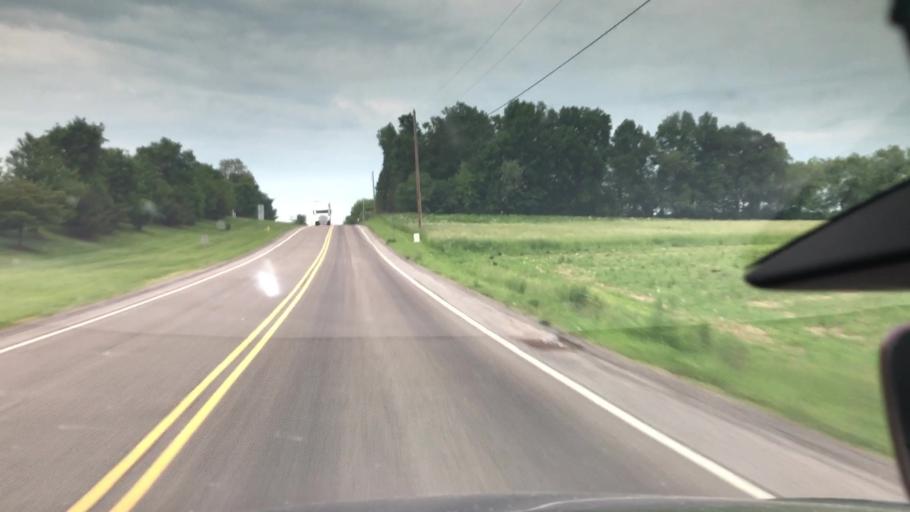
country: US
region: Pennsylvania
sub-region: Butler County
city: Saxonburg
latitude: 40.7308
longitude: -79.8531
